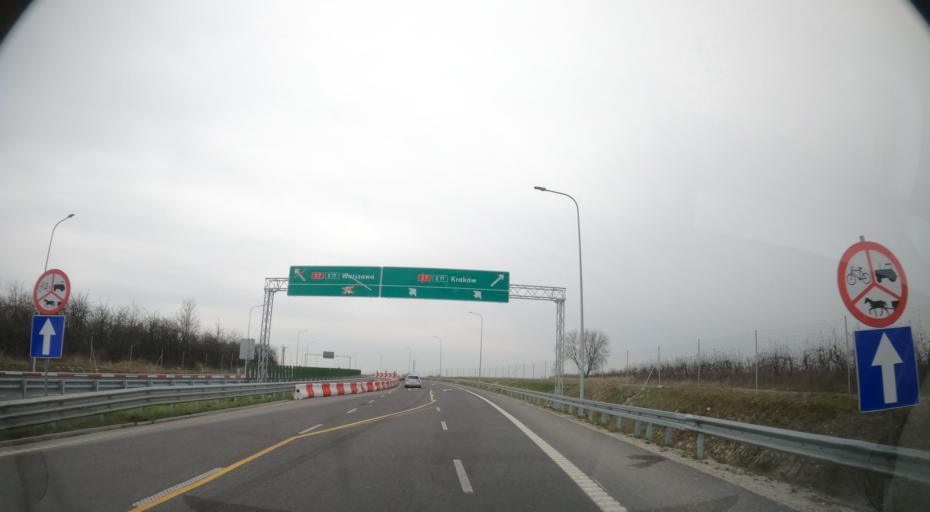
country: PL
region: Masovian Voivodeship
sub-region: Powiat piaseczynski
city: Tarczyn
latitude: 51.9534
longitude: 20.8413
